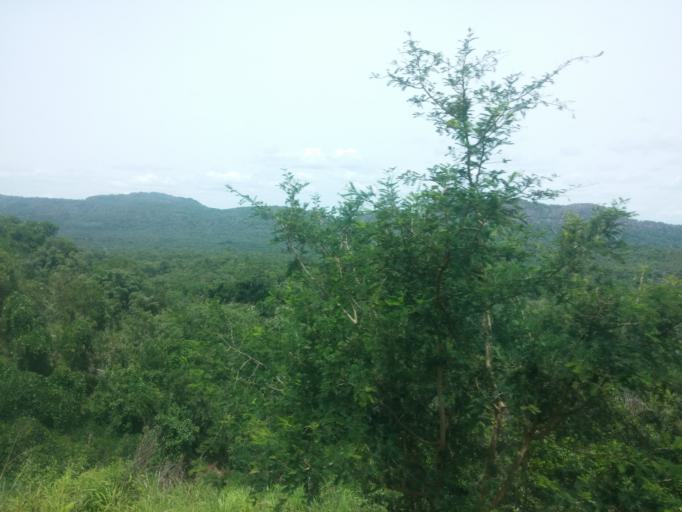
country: TG
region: Kara
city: Bafilo
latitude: 9.2557
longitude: 1.2225
